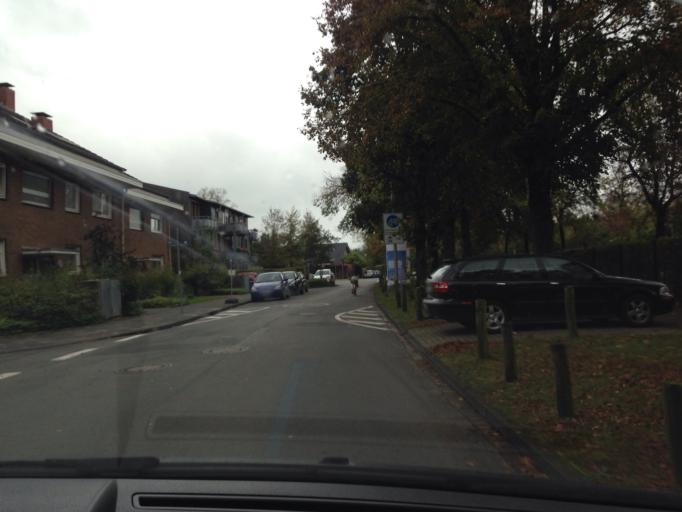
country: DE
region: North Rhine-Westphalia
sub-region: Regierungsbezirk Munster
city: Muenster
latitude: 51.9592
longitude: 7.5893
